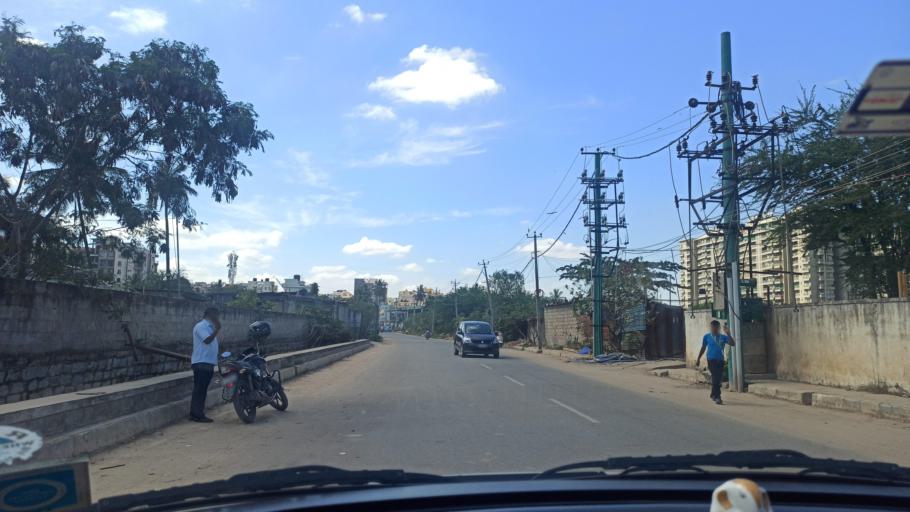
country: IN
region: Karnataka
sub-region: Bangalore Urban
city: Bangalore
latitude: 12.9303
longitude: 77.6817
